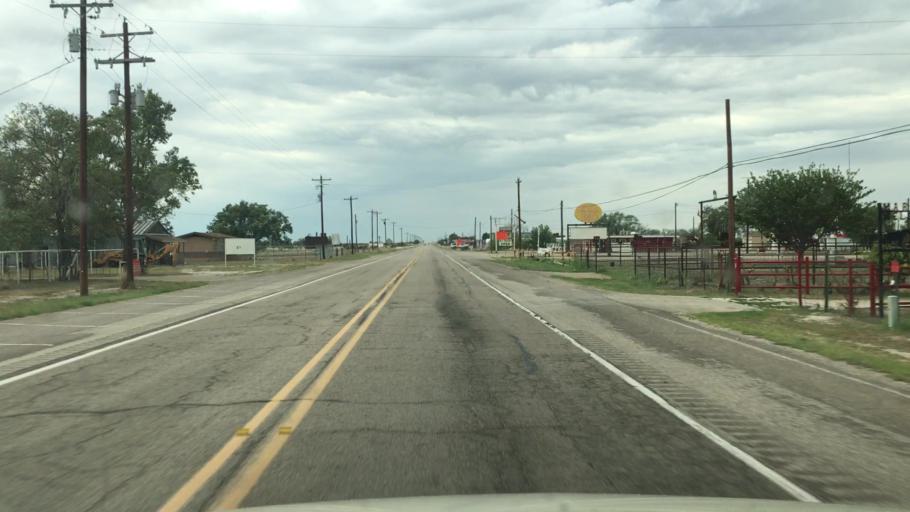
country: US
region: New Mexico
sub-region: Lea County
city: Lovington
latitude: 33.2570
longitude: -103.3382
